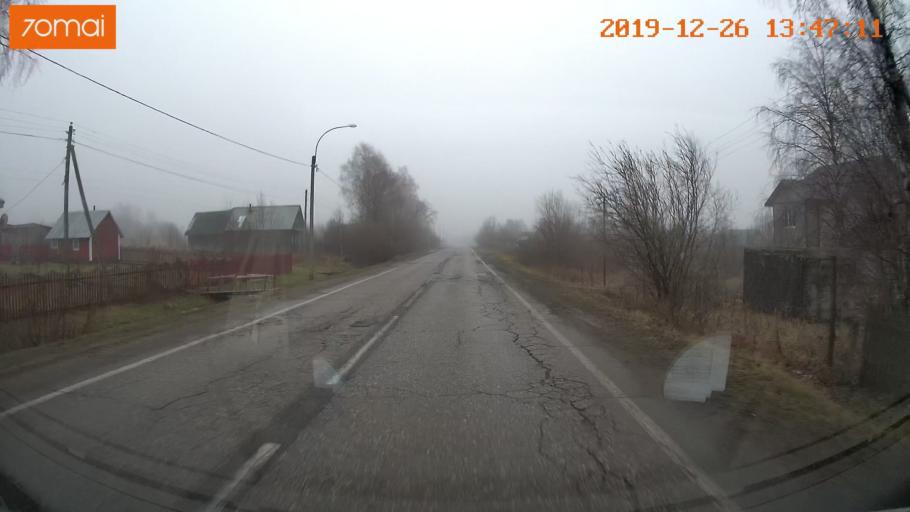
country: RU
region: Vologda
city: Sheksna
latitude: 58.6867
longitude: 38.5317
